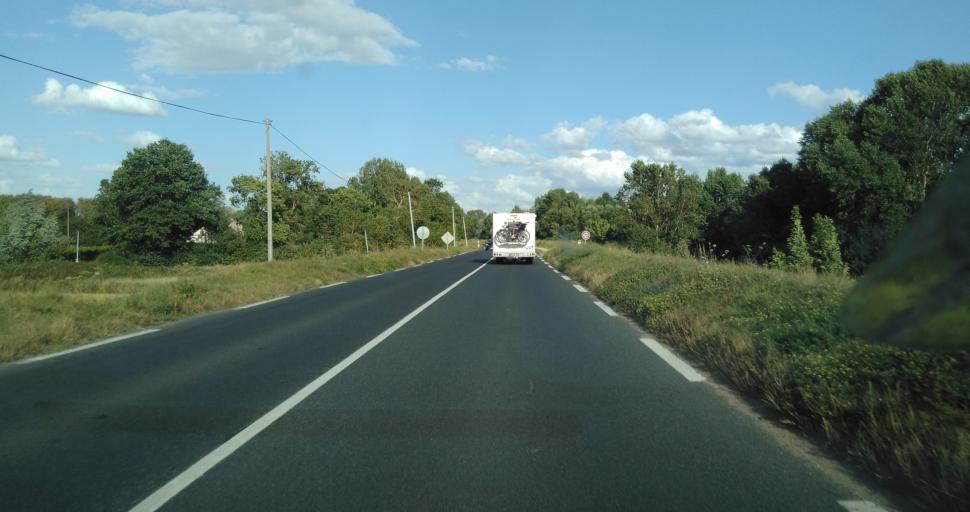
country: FR
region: Centre
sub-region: Departement d'Indre-et-Loire
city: Noizay
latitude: 47.4024
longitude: 0.9116
